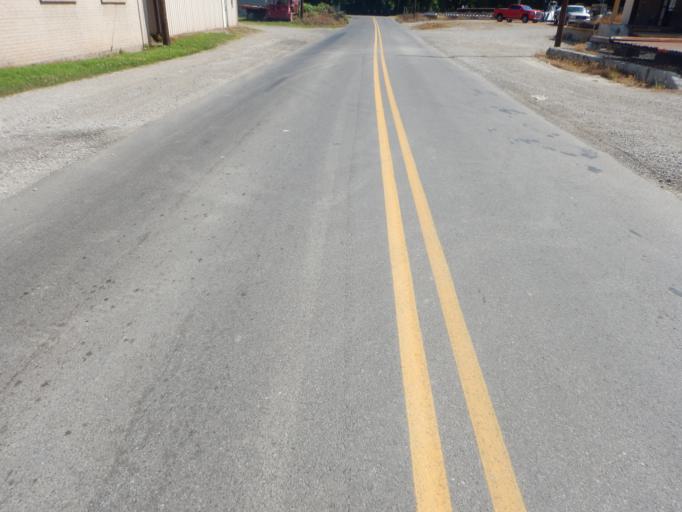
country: US
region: Ohio
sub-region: Muskingum County
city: Zanesville
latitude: 39.9432
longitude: -82.0260
